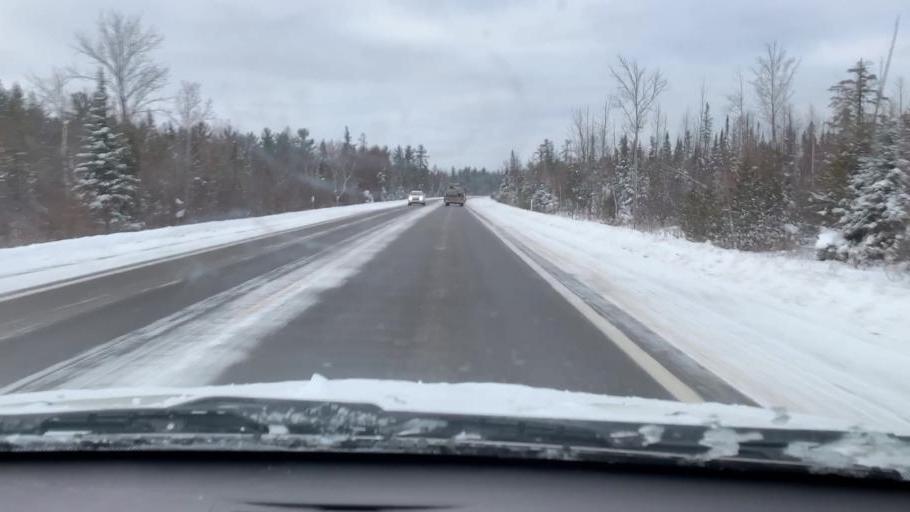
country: US
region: Michigan
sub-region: Kalkaska County
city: Kalkaska
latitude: 44.7043
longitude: -85.2003
